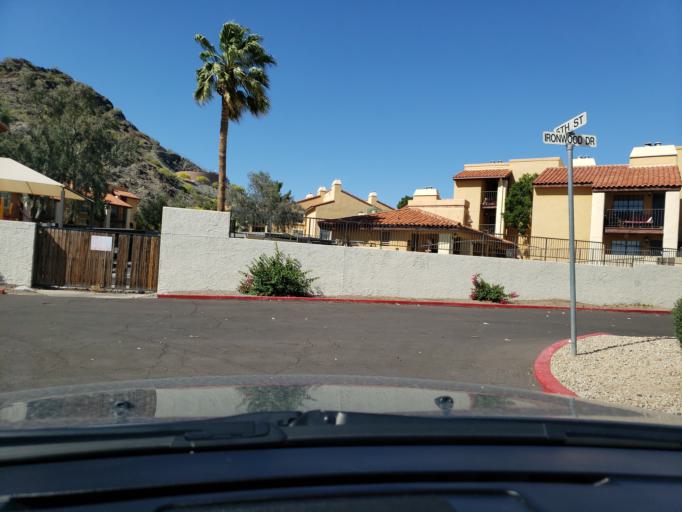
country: US
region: Arizona
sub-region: Maricopa County
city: Glendale
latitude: 33.5758
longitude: -112.0673
